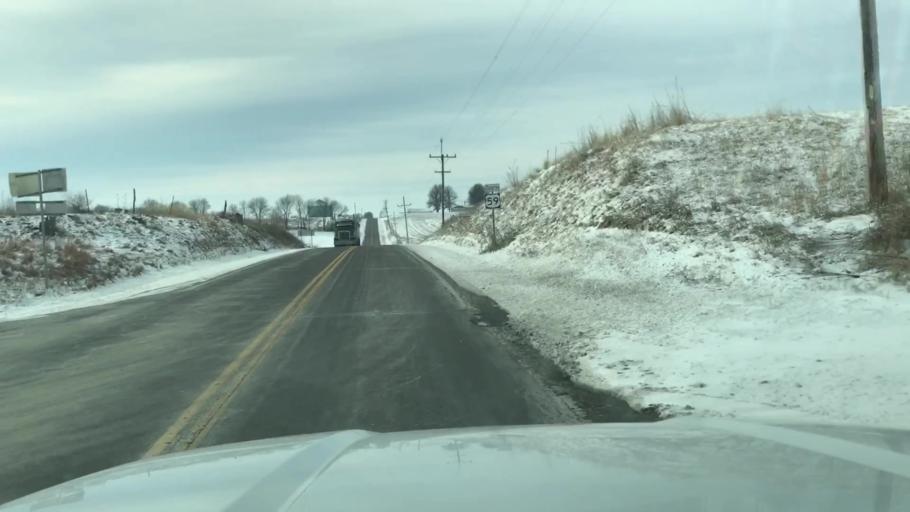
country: US
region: Missouri
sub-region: Holt County
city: Oregon
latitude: 40.0648
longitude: -95.1356
